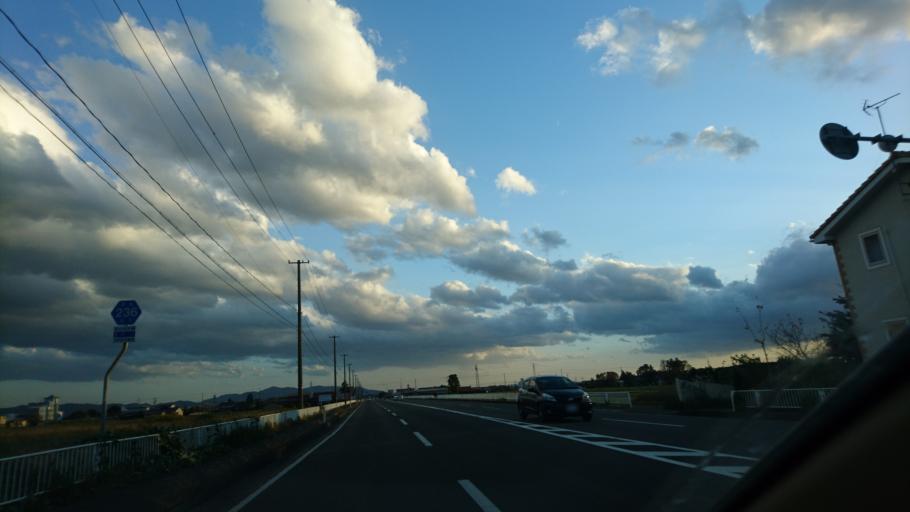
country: JP
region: Iwate
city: Mizusawa
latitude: 39.1635
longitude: 141.1327
